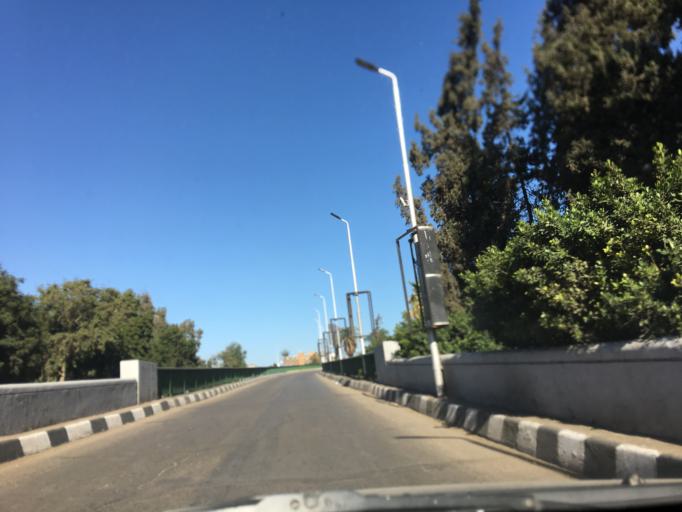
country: EG
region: Muhafazat al Qahirah
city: Cairo
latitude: 30.0473
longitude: 31.2270
